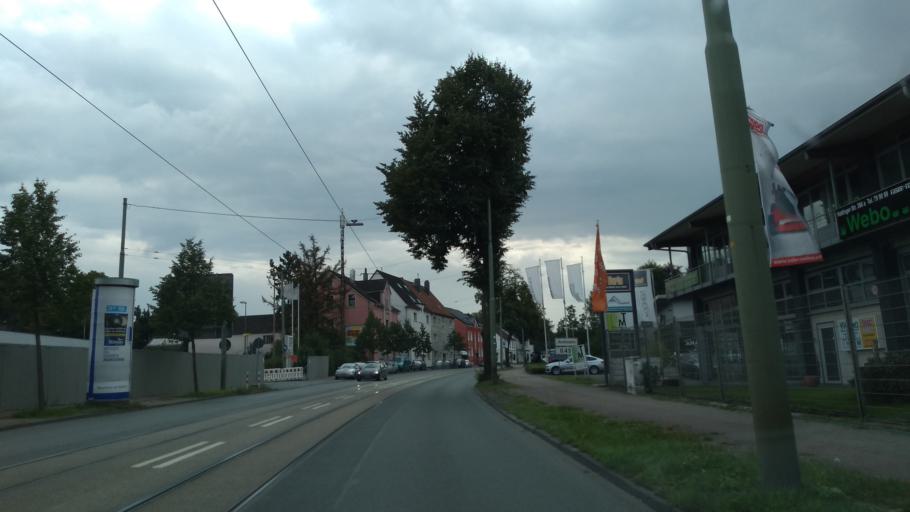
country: DE
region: North Rhine-Westphalia
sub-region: Regierungsbezirk Arnsberg
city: Bochum
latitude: 51.4459
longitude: 7.1946
